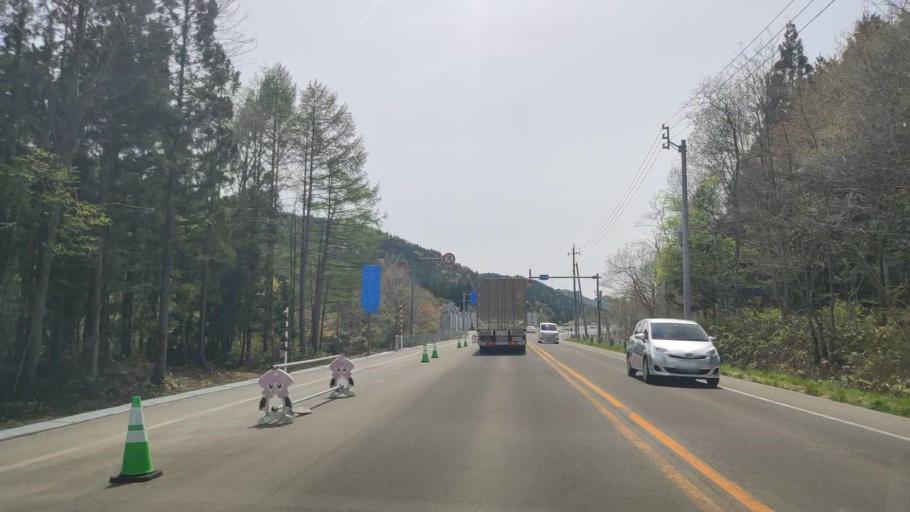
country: JP
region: Aomori
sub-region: Misawa Shi
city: Inuotose
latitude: 40.7852
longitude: 141.0689
